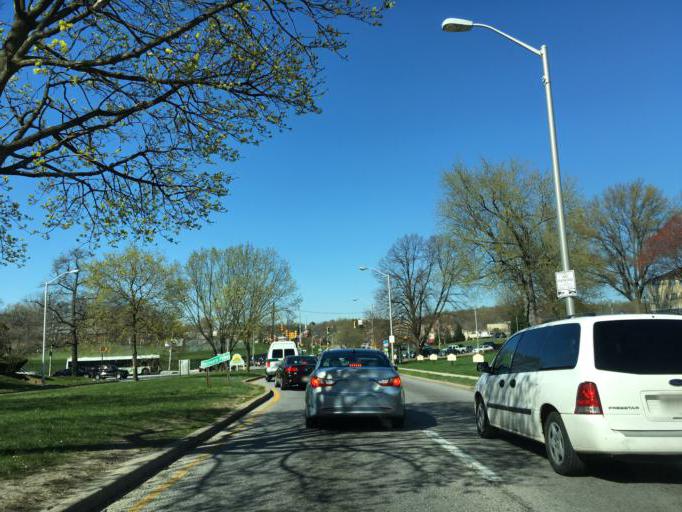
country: US
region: Maryland
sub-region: Baltimore County
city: Towson
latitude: 39.3651
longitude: -76.5860
